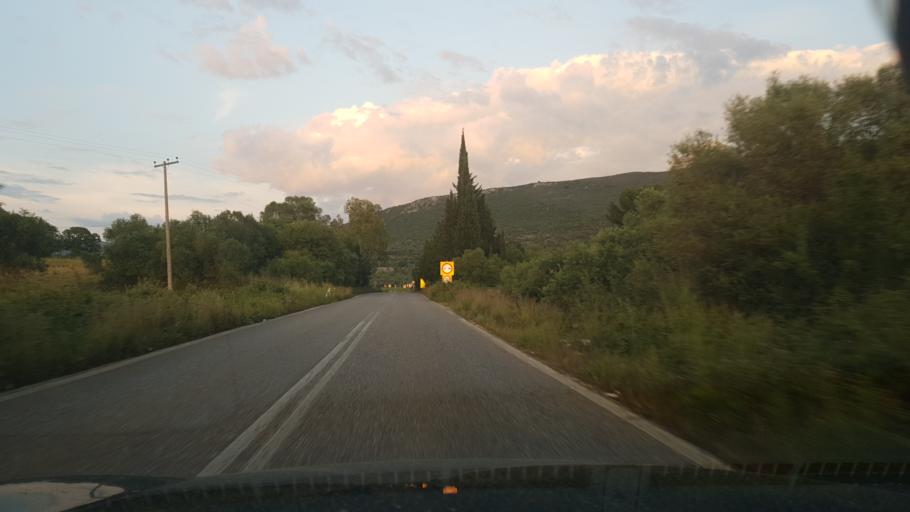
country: GR
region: West Greece
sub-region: Nomos Aitolias kai Akarnanias
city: Vonitsa
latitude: 38.8973
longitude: 20.8689
